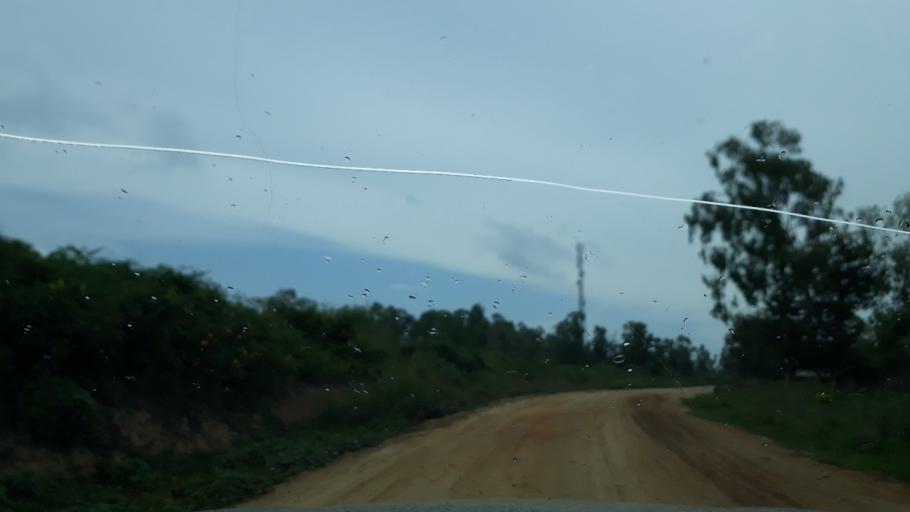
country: CD
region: Eastern Province
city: Bunia
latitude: 1.5905
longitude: 30.2549
